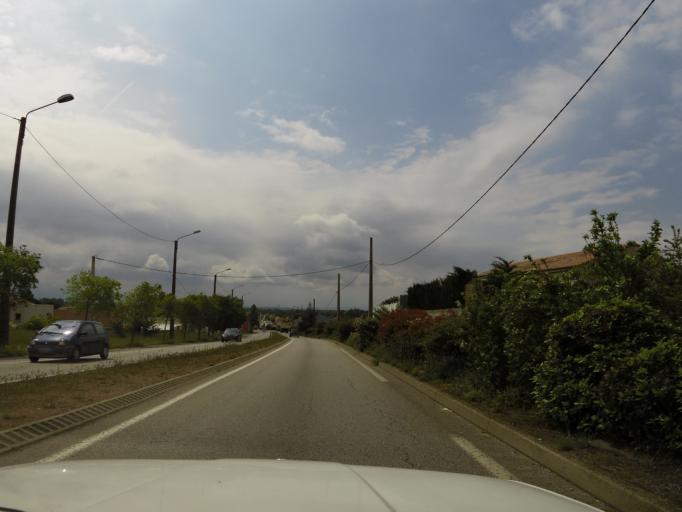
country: FR
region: Rhone-Alpes
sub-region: Departement de la Drome
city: La Roche-de-Glun
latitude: 45.0113
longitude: 4.8692
